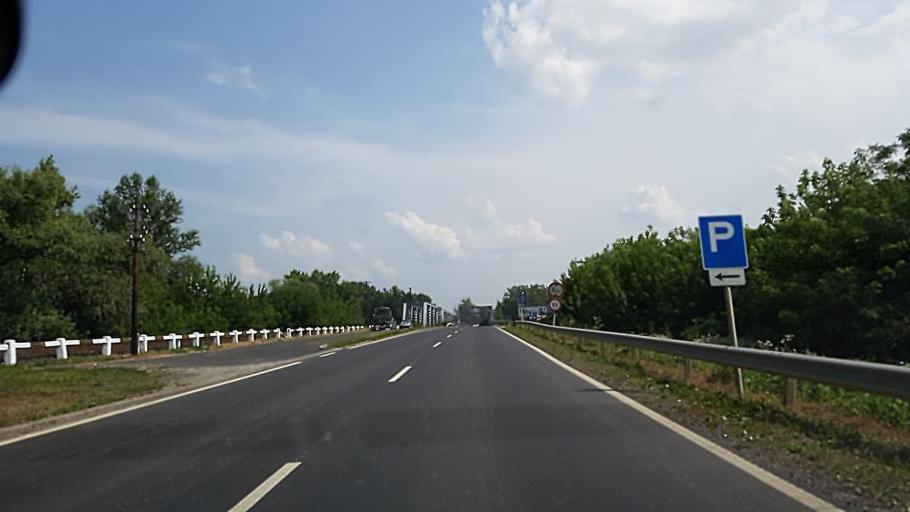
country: HU
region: Jasz-Nagykun-Szolnok
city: Tiszafured
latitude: 47.6423
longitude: 20.7255
